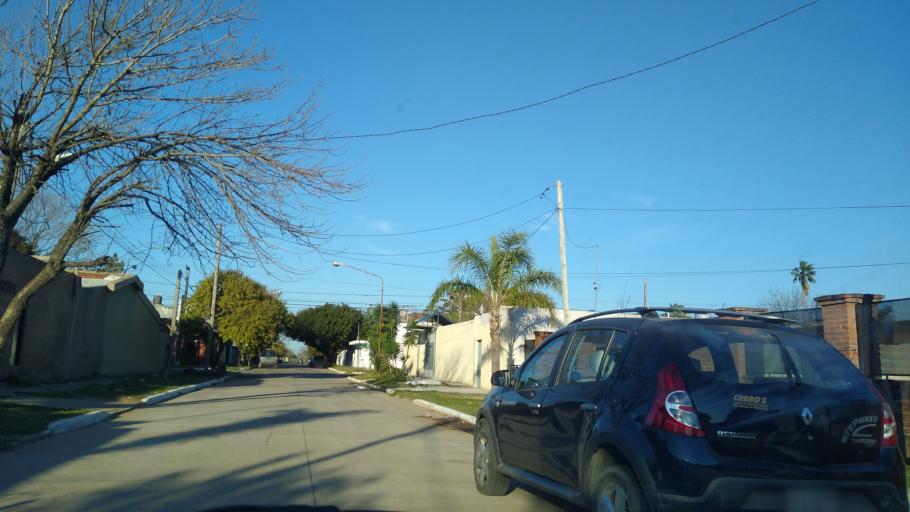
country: AR
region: Chaco
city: Barranqueras
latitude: -27.4793
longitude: -58.9503
